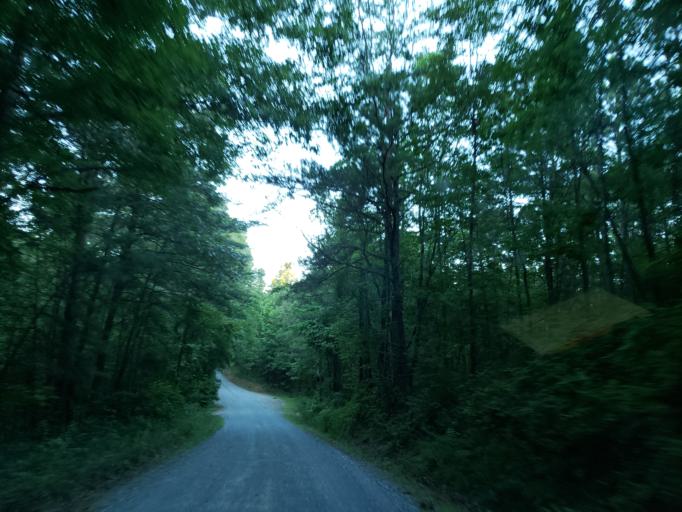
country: US
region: Georgia
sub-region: Bartow County
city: Euharlee
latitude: 34.0733
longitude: -84.8607
